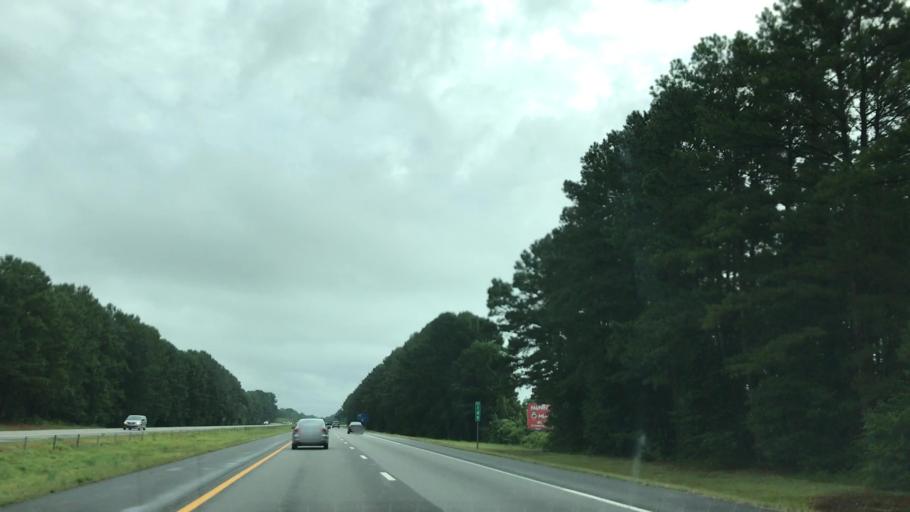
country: US
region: North Carolina
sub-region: Nash County
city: Red Oak
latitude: 36.1180
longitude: -77.8008
